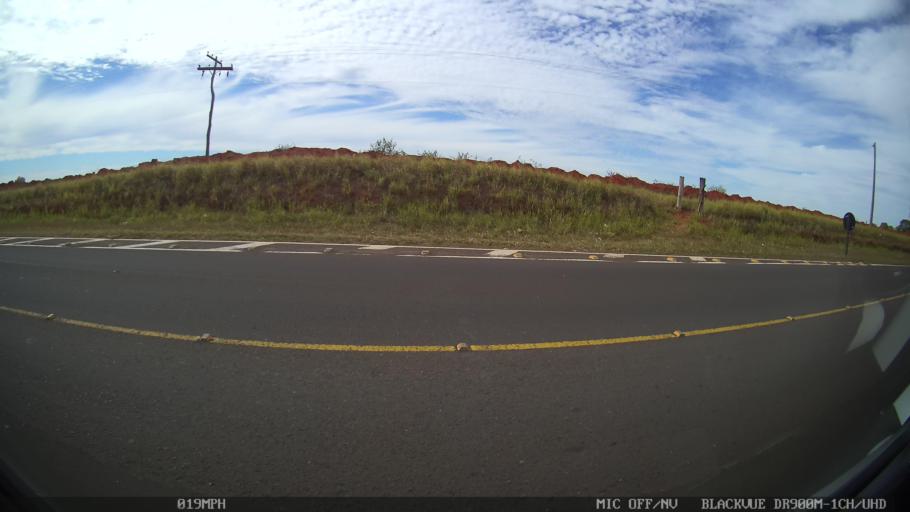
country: BR
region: Sao Paulo
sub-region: Catanduva
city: Catanduva
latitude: -21.1609
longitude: -48.9629
